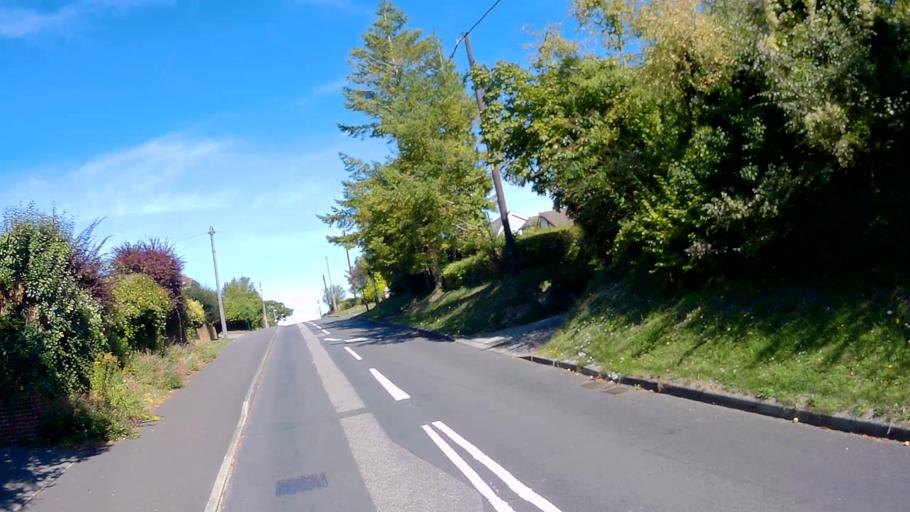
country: GB
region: England
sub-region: Hampshire
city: Basingstoke
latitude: 51.2557
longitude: -1.1379
